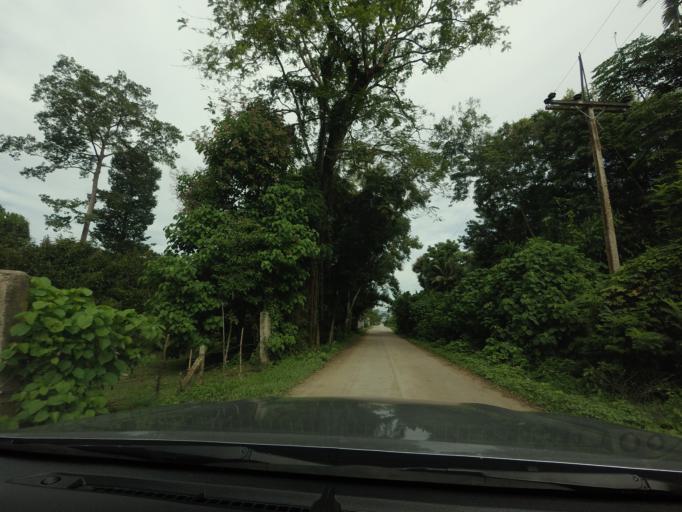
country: TH
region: Nakhon Si Thammarat
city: Phra Phrom
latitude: 8.2826
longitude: 99.9100
